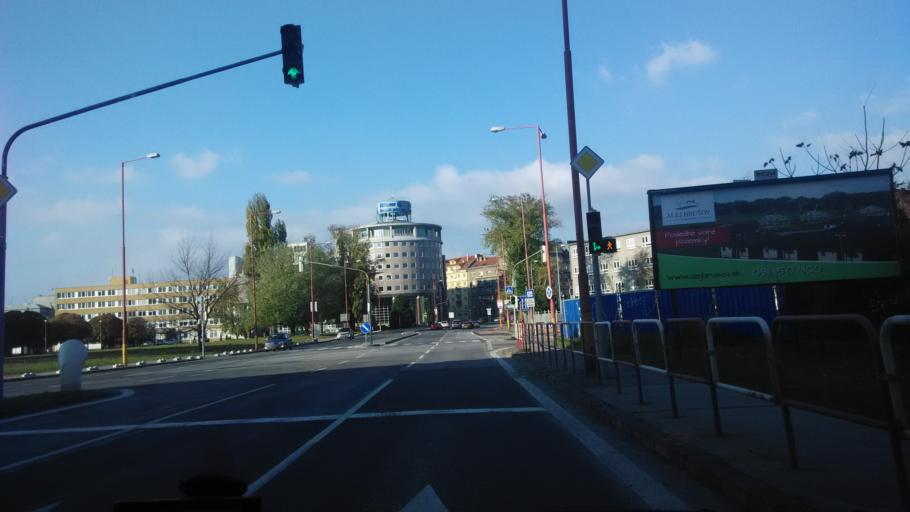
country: SK
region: Bratislavsky
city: Bratislava
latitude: 48.1426
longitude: 17.1250
